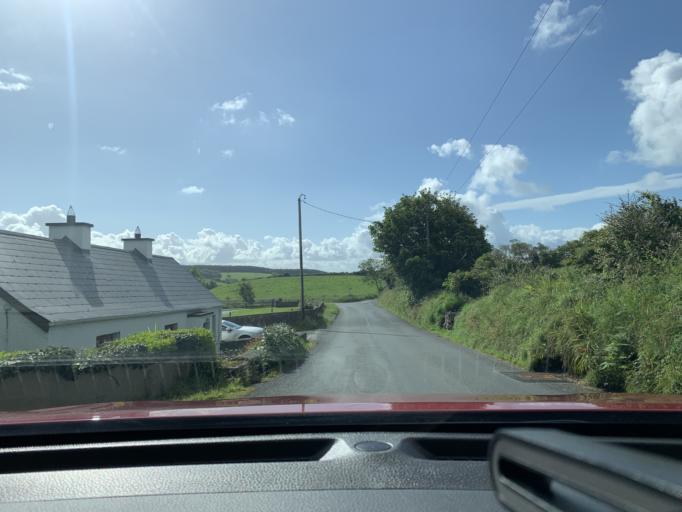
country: IE
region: Connaught
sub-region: Sligo
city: Strandhill
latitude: 54.3545
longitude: -8.6054
